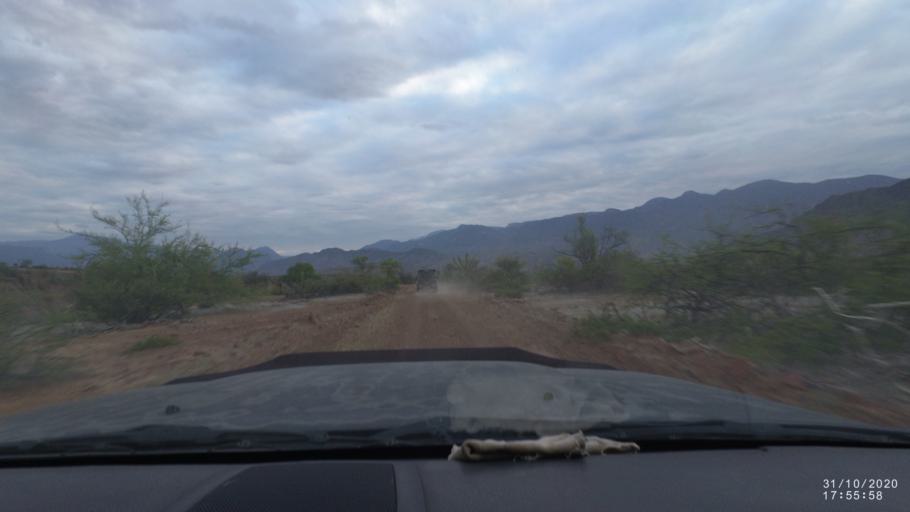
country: BO
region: Chuquisaca
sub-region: Provincia Zudanez
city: Mojocoya
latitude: -18.6479
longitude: -64.5288
